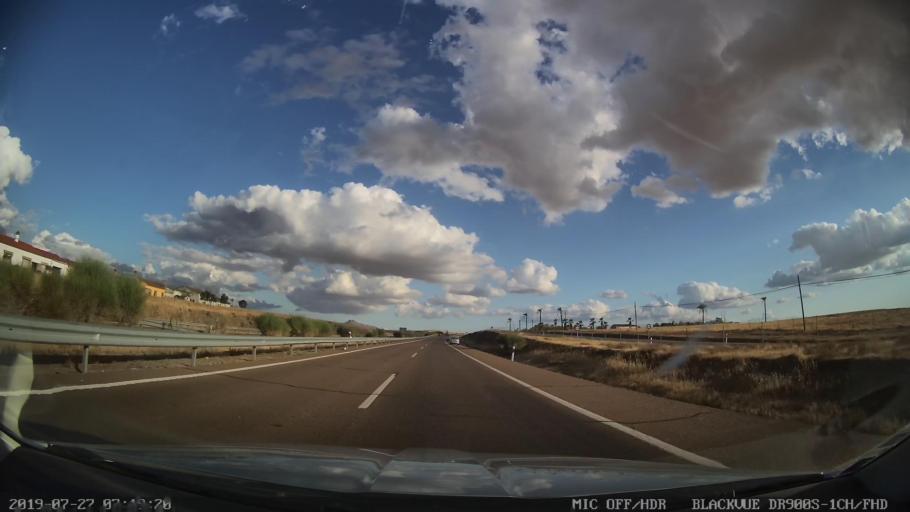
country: ES
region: Extremadura
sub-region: Provincia de Caceres
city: Trujillo
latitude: 39.4007
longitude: -5.8892
